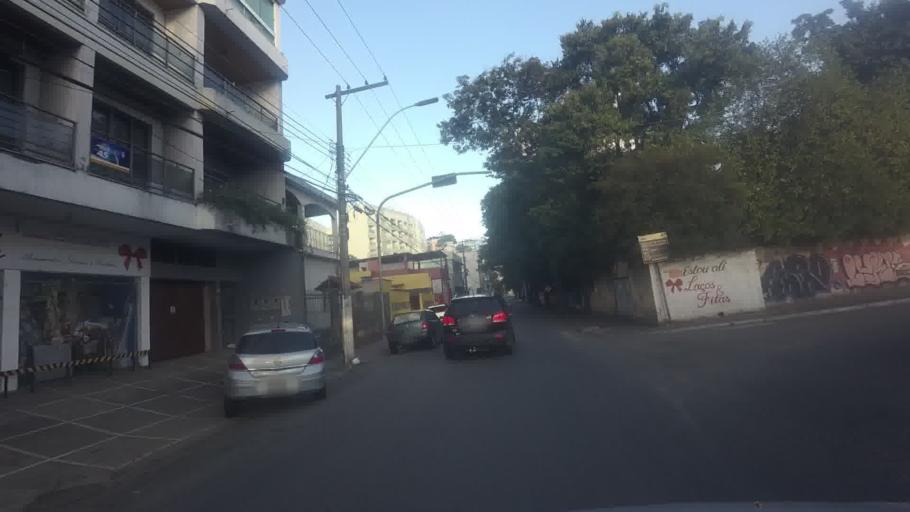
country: BR
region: Espirito Santo
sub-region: Cachoeiro De Itapemirim
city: Cachoeiro de Itapemirim
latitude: -20.8467
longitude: -41.1129
